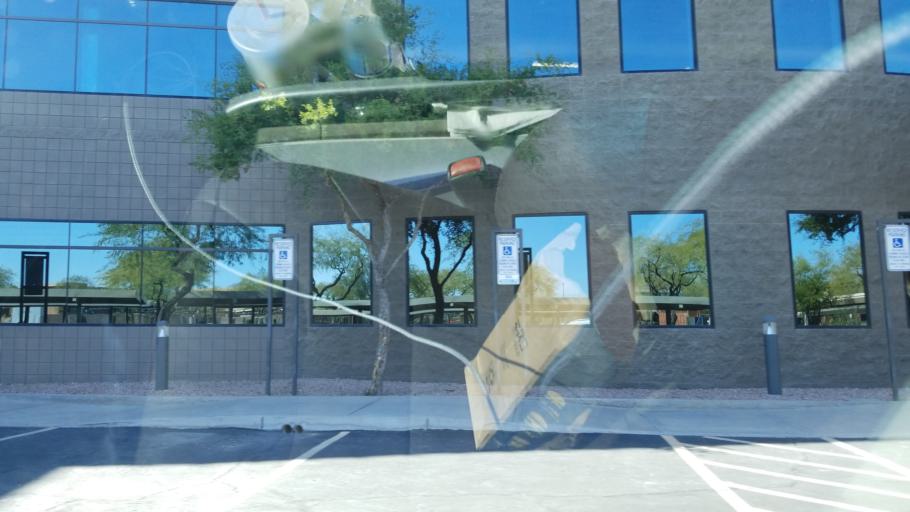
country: US
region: Arizona
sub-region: Maricopa County
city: Paradise Valley
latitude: 33.6195
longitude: -111.9320
